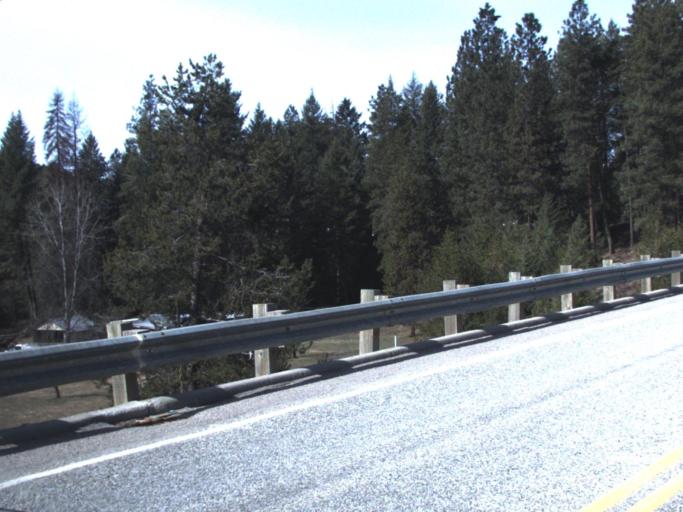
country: US
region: Washington
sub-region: Stevens County
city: Colville
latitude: 48.5408
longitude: -117.8402
